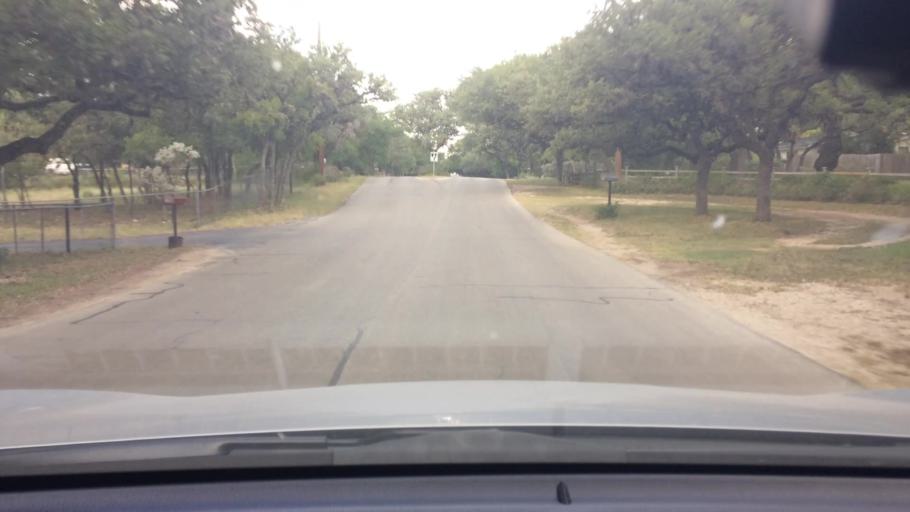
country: US
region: Texas
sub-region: Bexar County
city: Hollywood Park
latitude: 29.5563
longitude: -98.4683
